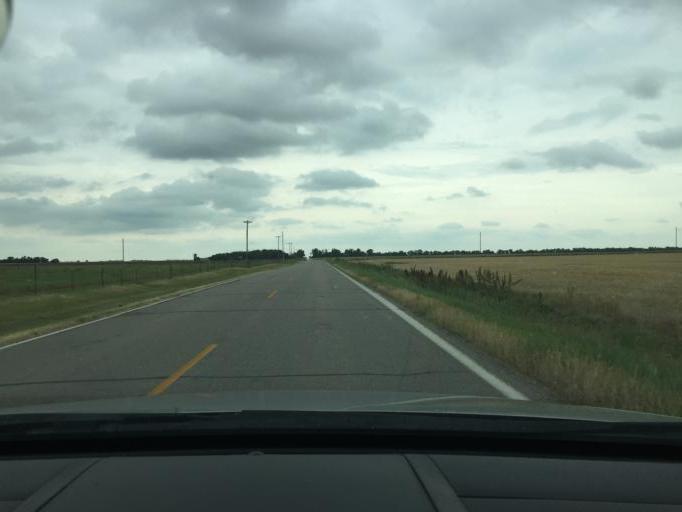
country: US
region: Kansas
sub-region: Reno County
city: South Hutchinson
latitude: 38.0116
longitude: -98.0136
